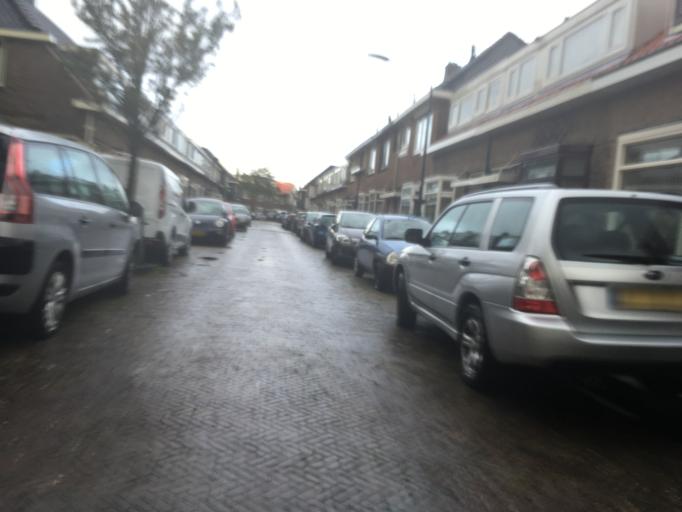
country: NL
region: North Holland
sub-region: Gemeente Haarlem
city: Haarlem
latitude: 52.3779
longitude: 4.6559
